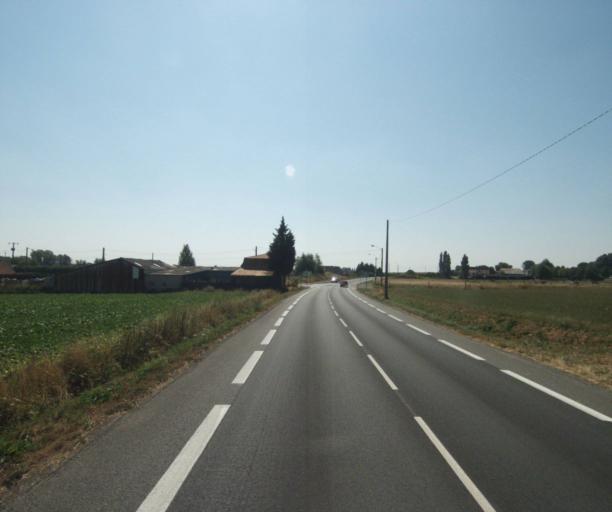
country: FR
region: Nord-Pas-de-Calais
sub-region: Departement du Nord
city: Bousbecque
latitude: 50.7568
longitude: 3.0782
